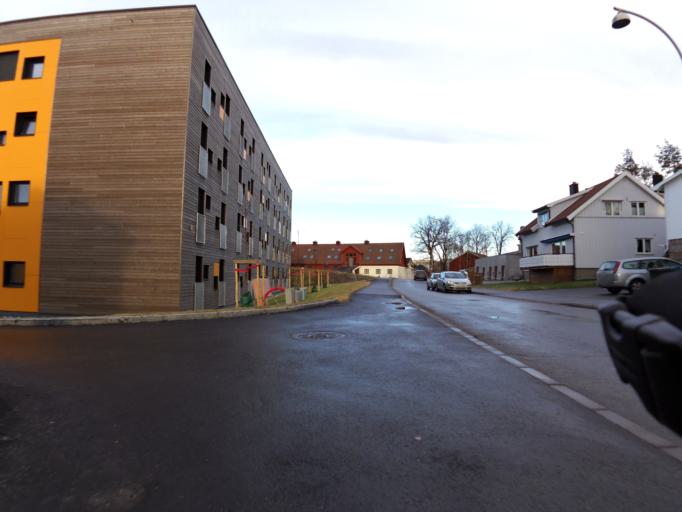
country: NO
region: Ostfold
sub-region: Fredrikstad
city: Fredrikstad
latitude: 59.2101
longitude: 10.9324
